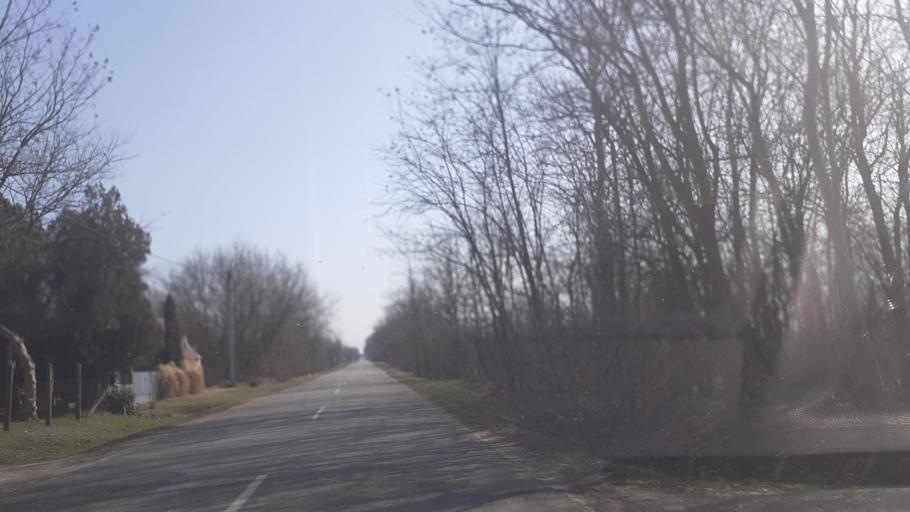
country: HU
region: Pest
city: Taborfalva
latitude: 47.0401
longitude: 19.4416
